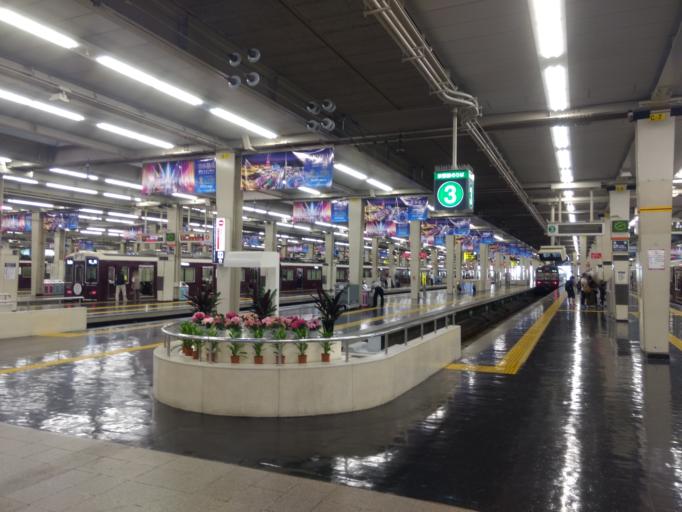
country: JP
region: Osaka
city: Osaka-shi
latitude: 34.7052
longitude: 135.4989
